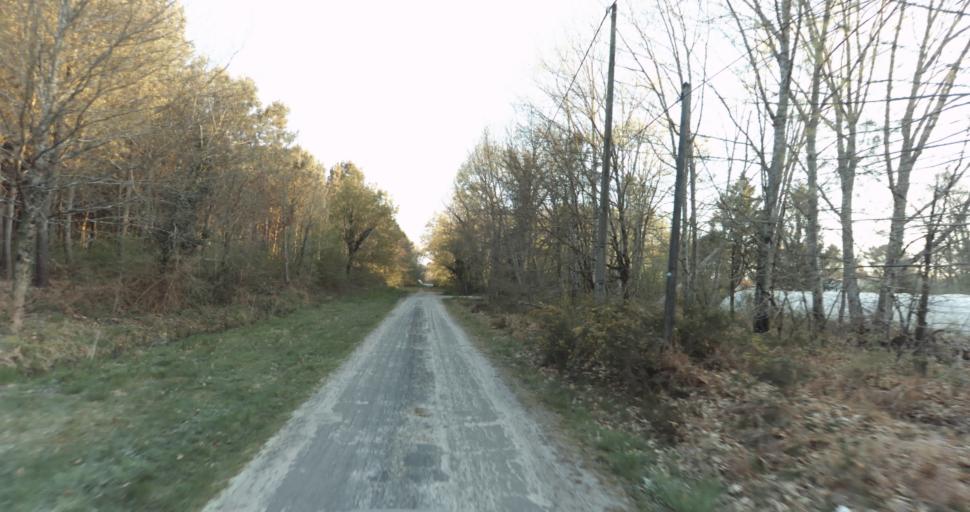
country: FR
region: Aquitaine
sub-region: Departement de la Gironde
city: Martignas-sur-Jalle
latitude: 44.8127
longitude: -0.7580
